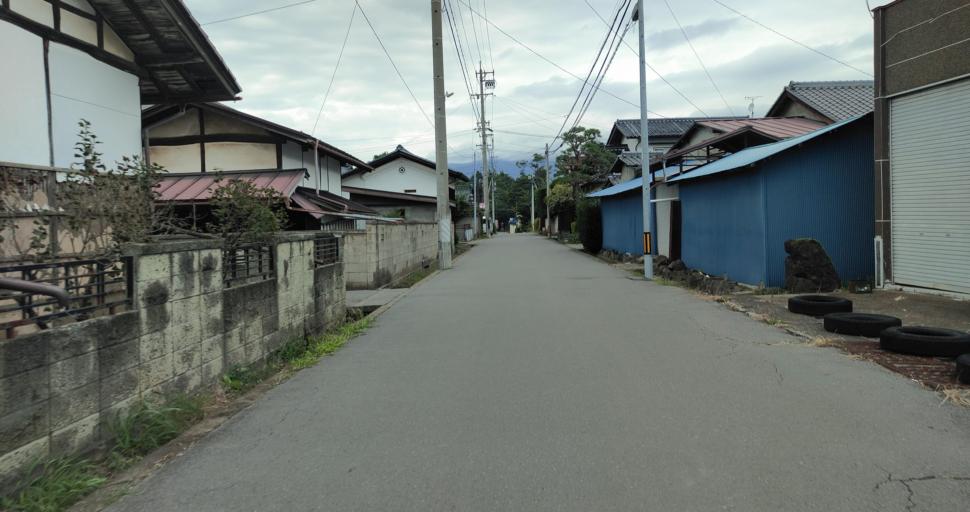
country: JP
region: Nagano
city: Komoro
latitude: 36.2919
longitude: 138.4584
